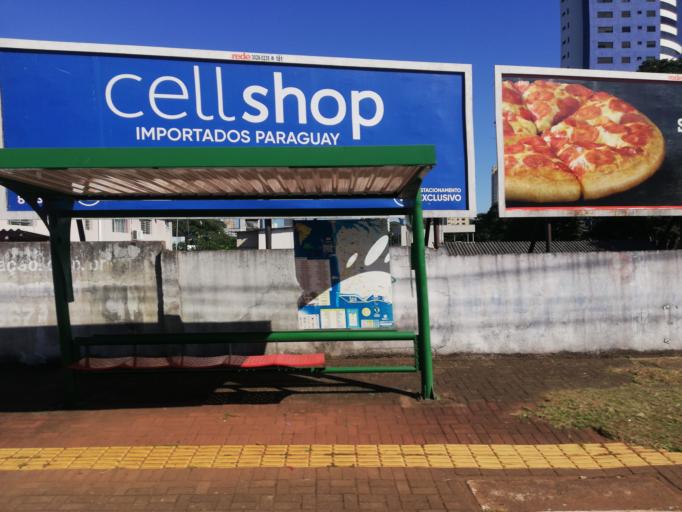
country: BR
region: Parana
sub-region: Foz Do Iguacu
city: Foz do Iguacu
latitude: -25.5453
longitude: -54.5765
